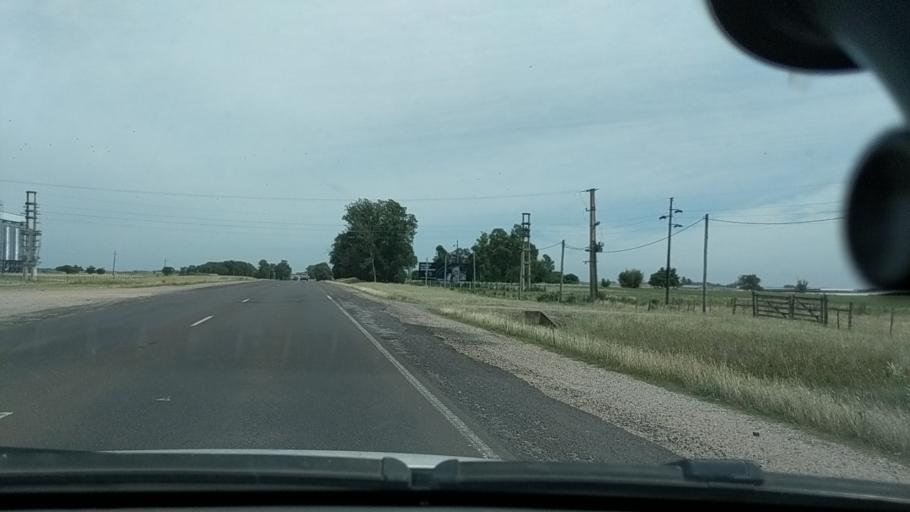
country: UY
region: Durazno
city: Durazno
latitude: -33.4956
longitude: -56.4282
